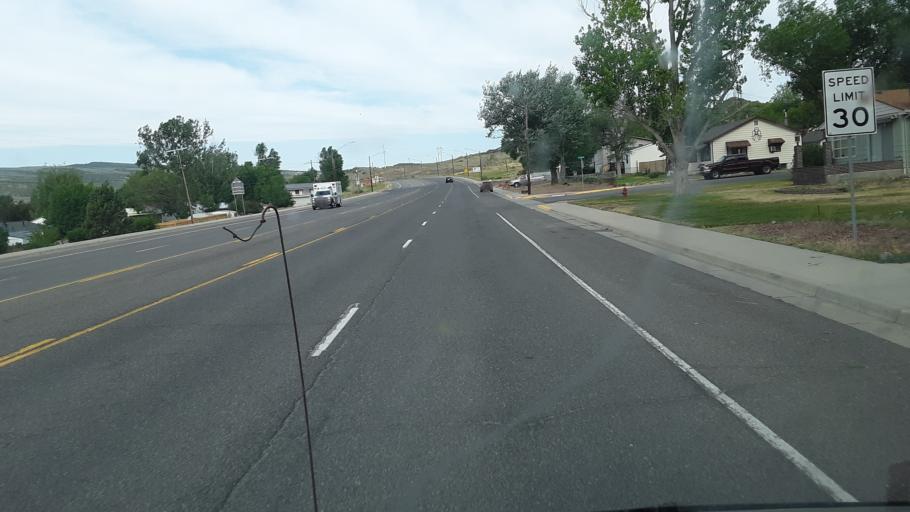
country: US
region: Wyoming
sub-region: Hot Springs County
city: Thermopolis
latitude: 43.6464
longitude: -108.2232
